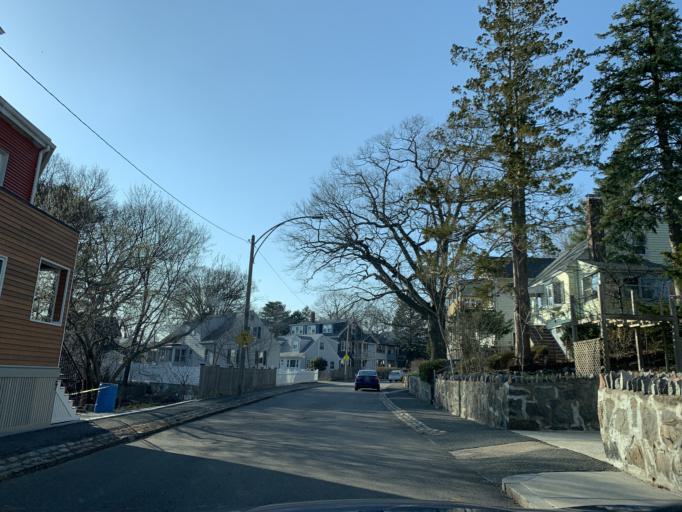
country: US
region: Massachusetts
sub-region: Suffolk County
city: Jamaica Plain
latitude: 42.2889
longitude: -71.1132
